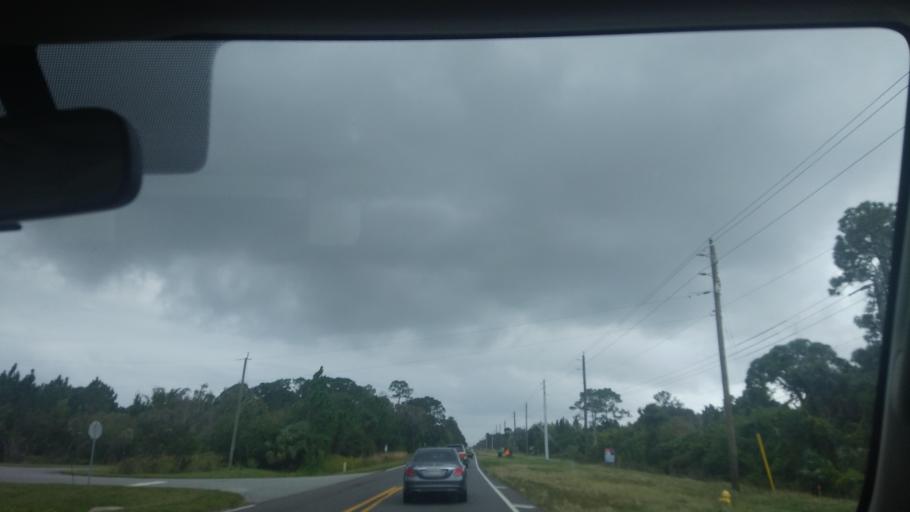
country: US
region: Florida
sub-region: Brevard County
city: Malabar
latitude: 27.9784
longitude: -80.6225
